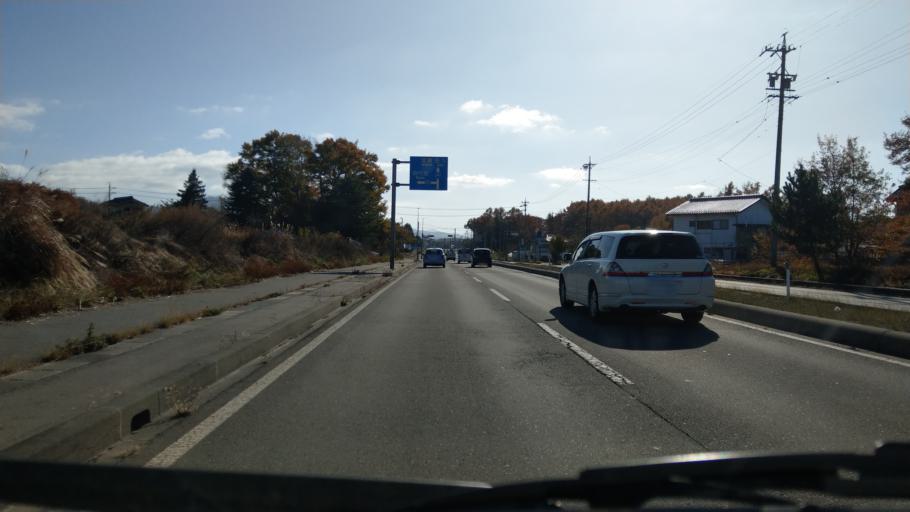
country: JP
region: Nagano
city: Komoro
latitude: 36.3050
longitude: 138.4606
